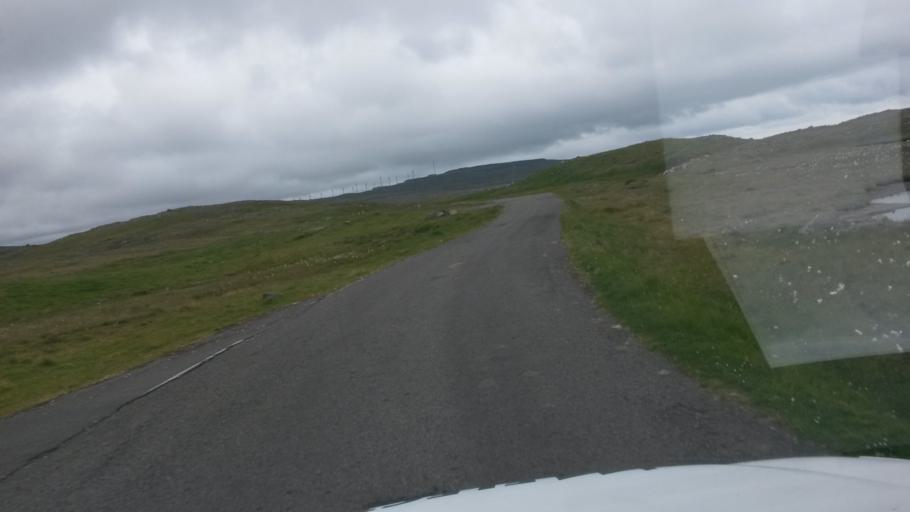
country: FO
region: Streymoy
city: Argir
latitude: 61.9929
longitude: -6.8490
